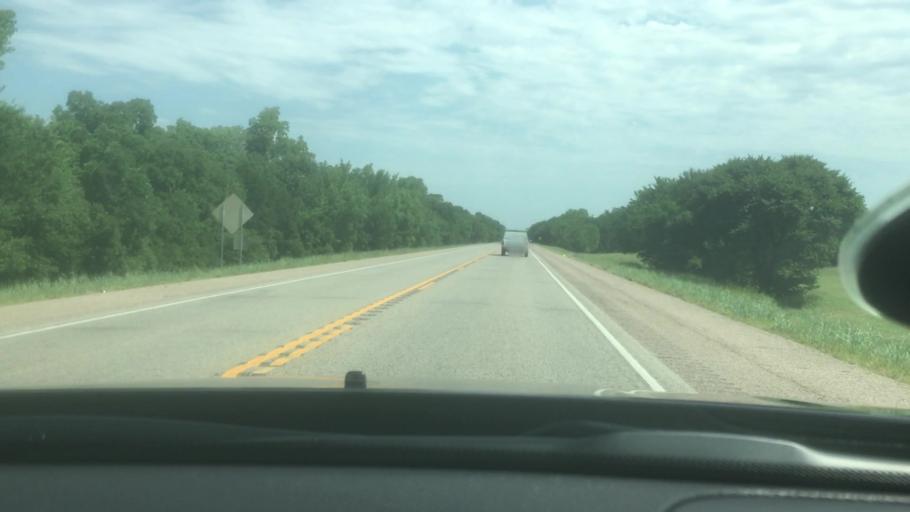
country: US
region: Oklahoma
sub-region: Seminole County
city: Maud
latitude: 35.0763
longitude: -96.9312
